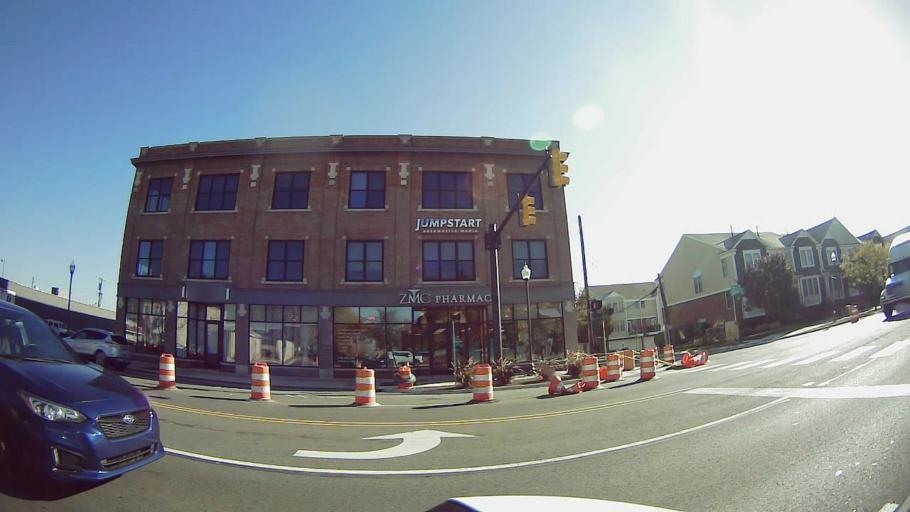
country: US
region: Michigan
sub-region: Oakland County
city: Royal Oak
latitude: 42.4806
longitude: -83.1441
